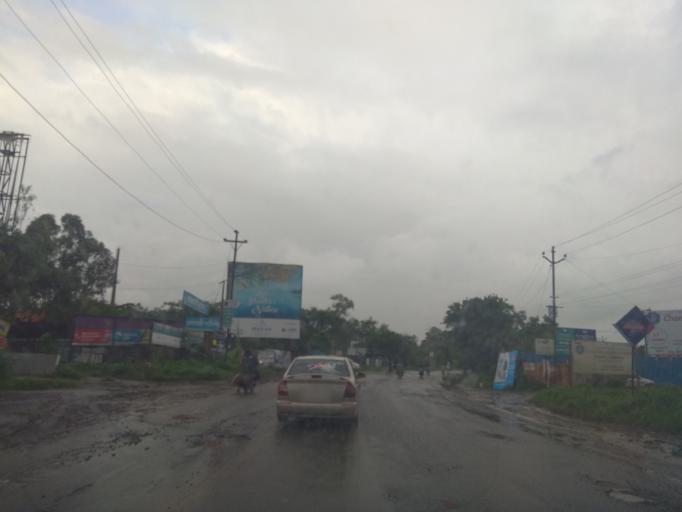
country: IN
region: Maharashtra
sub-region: Pune Division
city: Kharakvasla
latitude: 18.5111
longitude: 73.6838
